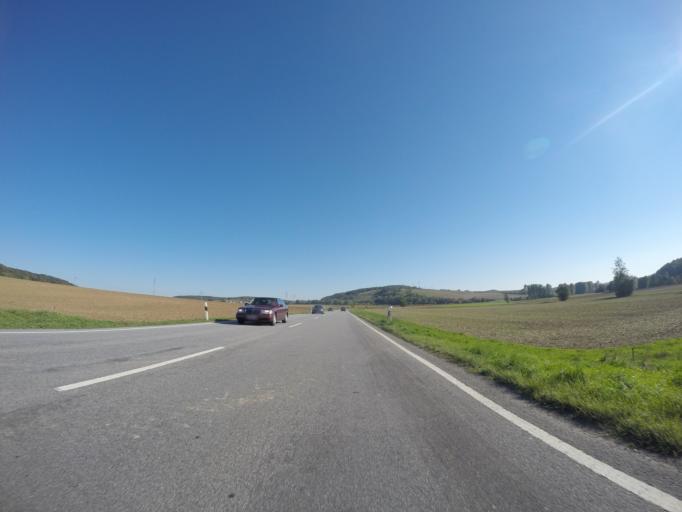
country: DE
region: Bavaria
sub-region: Regierungsbezirk Unterfranken
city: Uettingen
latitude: 49.7995
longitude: 9.7395
